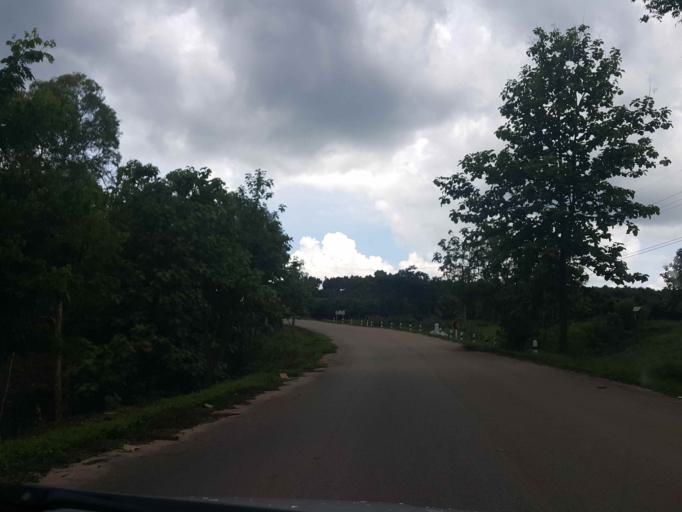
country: TH
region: Phayao
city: Dok Kham Tai
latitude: 18.9636
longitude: 100.0746
